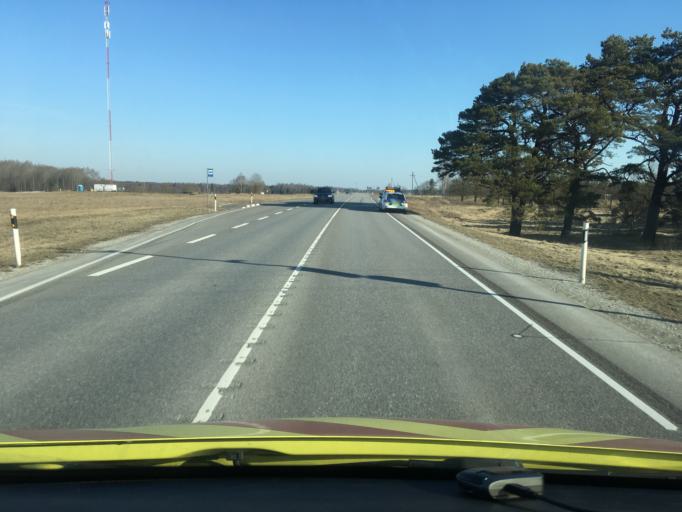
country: EE
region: Harju
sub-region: Saku vald
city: Saku
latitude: 59.2803
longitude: 24.7411
